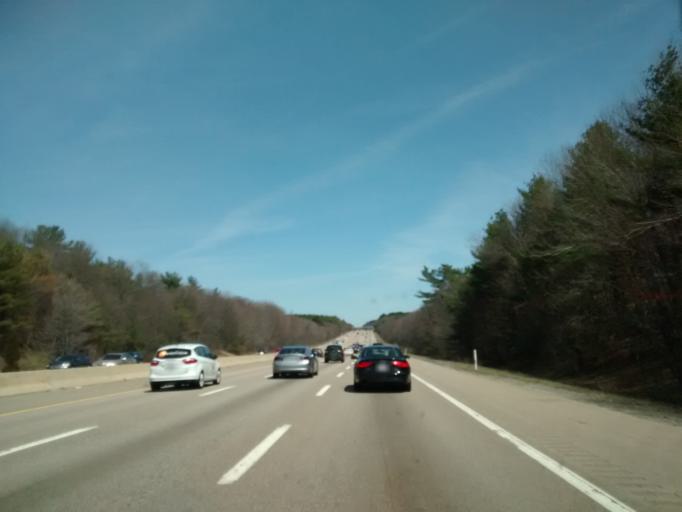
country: US
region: Massachusetts
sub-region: Worcester County
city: Cordaville
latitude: 42.2759
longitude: -71.5334
